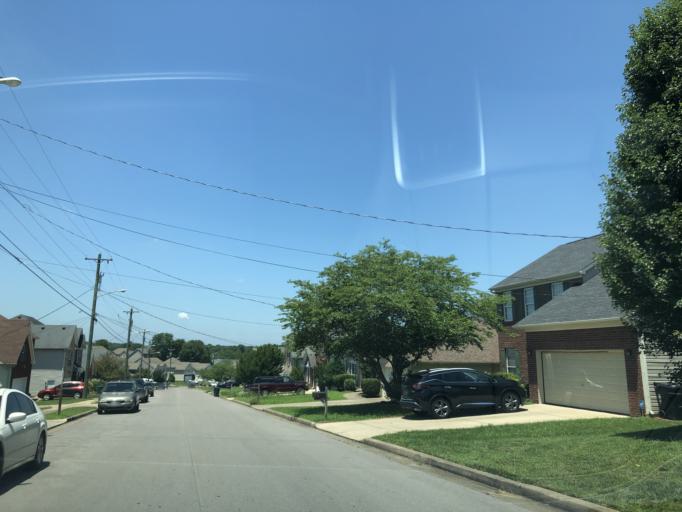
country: US
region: Tennessee
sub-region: Williamson County
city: Nolensville
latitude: 36.0198
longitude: -86.6524
